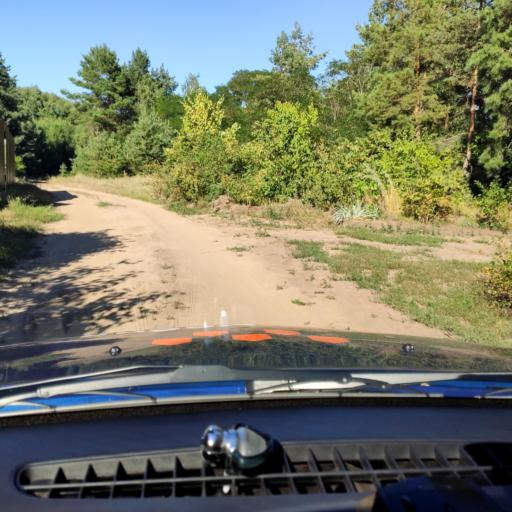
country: RU
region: Voronezj
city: Maslovka
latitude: 51.5411
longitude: 39.1643
